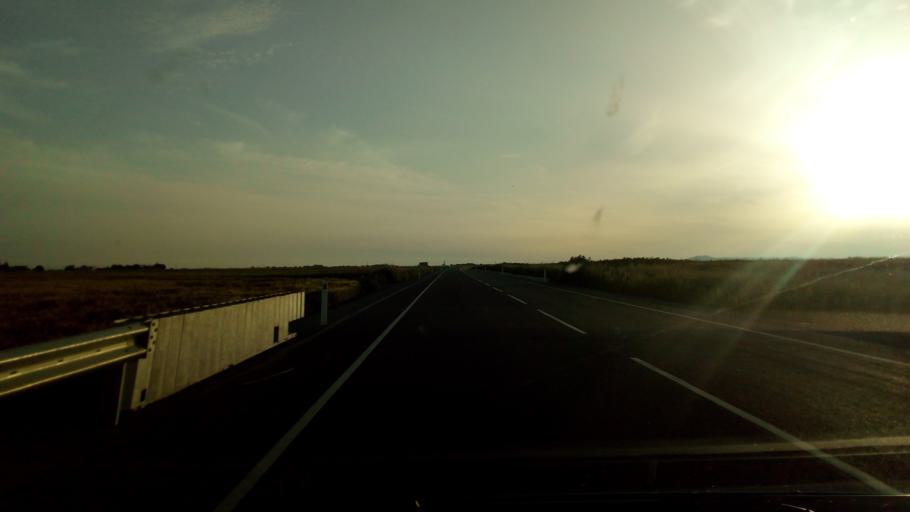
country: CY
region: Larnaka
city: Tersefanou
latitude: 34.8293
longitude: 33.5425
